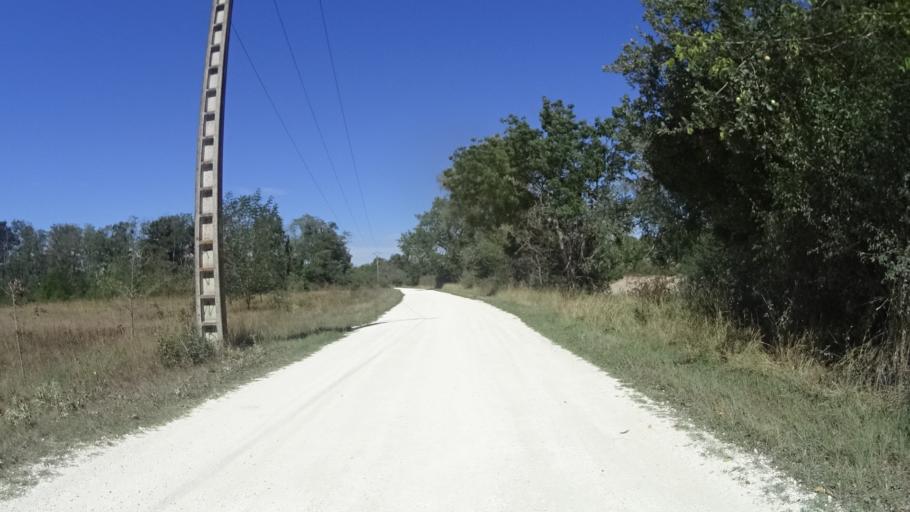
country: FR
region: Centre
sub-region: Departement du Loiret
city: Bonny-sur-Loire
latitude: 47.5396
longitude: 2.8421
